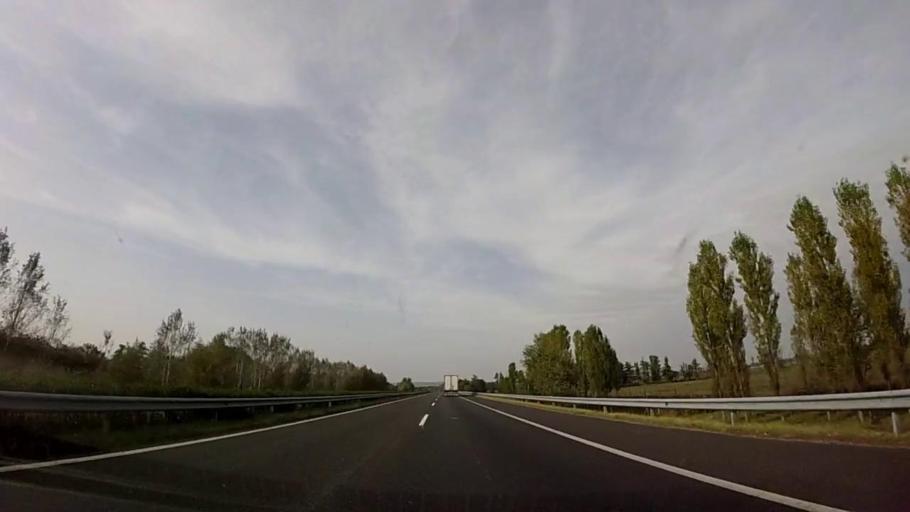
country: HU
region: Somogy
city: Kethely
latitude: 46.6875
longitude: 17.4162
